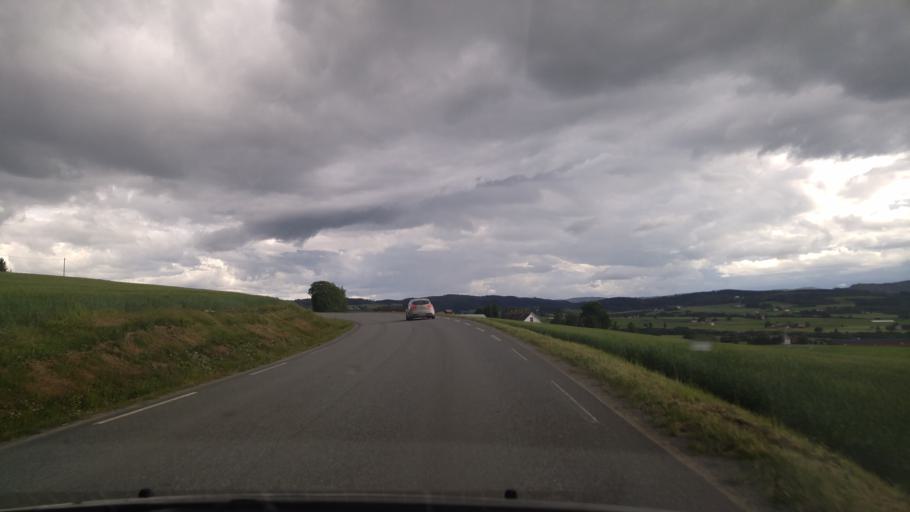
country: NO
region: Nord-Trondelag
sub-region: Levanger
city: Skogn
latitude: 63.6906
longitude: 11.2252
